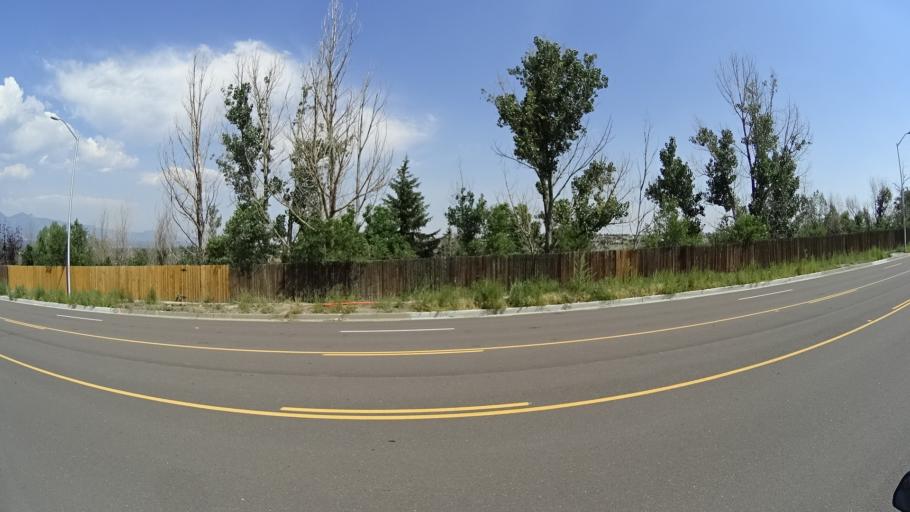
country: US
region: Colorado
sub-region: El Paso County
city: Colorado Springs
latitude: 38.9258
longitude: -104.7772
